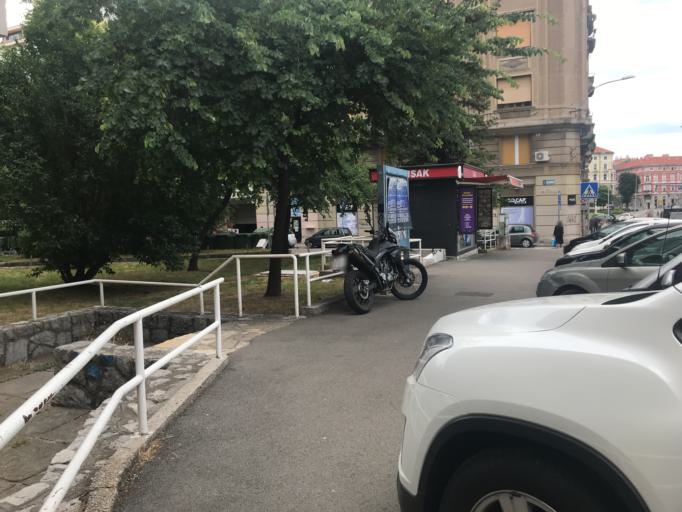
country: HR
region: Primorsko-Goranska
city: Drenova
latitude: 45.3276
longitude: 14.4463
